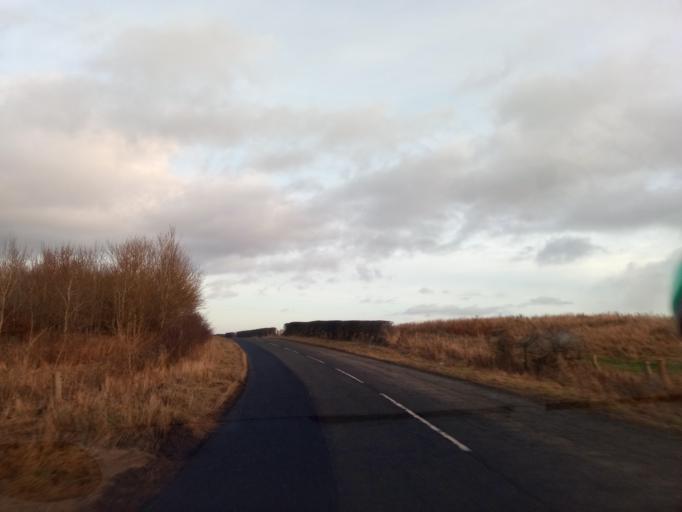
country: GB
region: Scotland
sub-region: The Scottish Borders
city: Melrose
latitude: 55.5520
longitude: -2.7486
